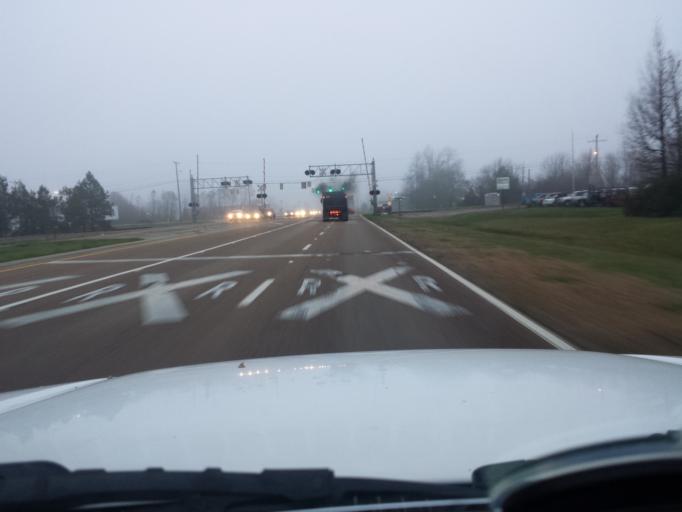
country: US
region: Mississippi
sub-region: Rankin County
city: Pearl
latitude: 32.2827
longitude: -90.1573
